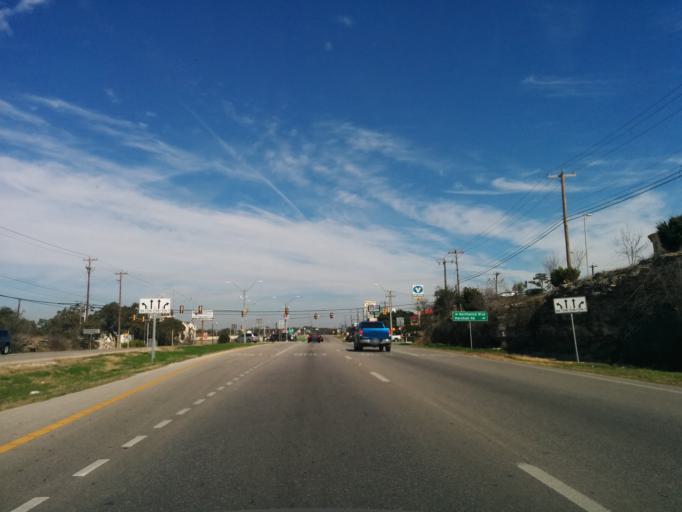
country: US
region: Texas
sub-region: Bexar County
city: Timberwood Park
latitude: 29.6597
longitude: -98.4501
